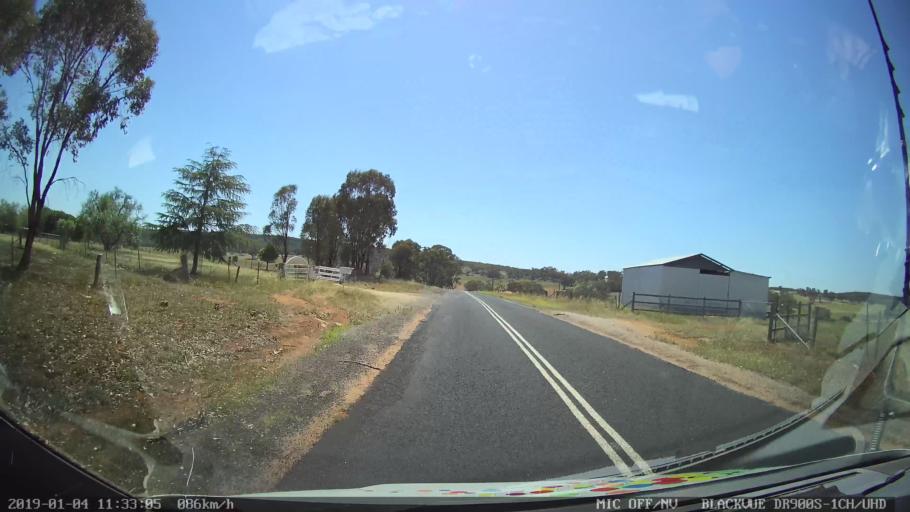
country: AU
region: New South Wales
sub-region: Cabonne
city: Molong
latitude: -33.0644
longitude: 148.8122
